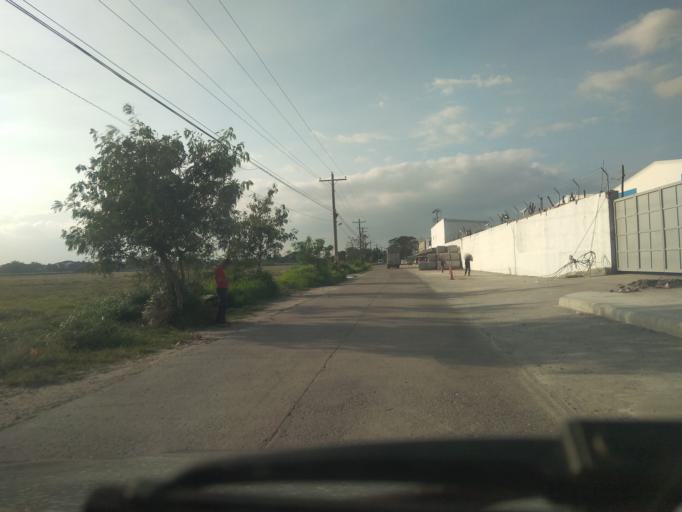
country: PH
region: Central Luzon
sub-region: Province of Pampanga
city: Malino
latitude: 15.1066
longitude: 120.6732
